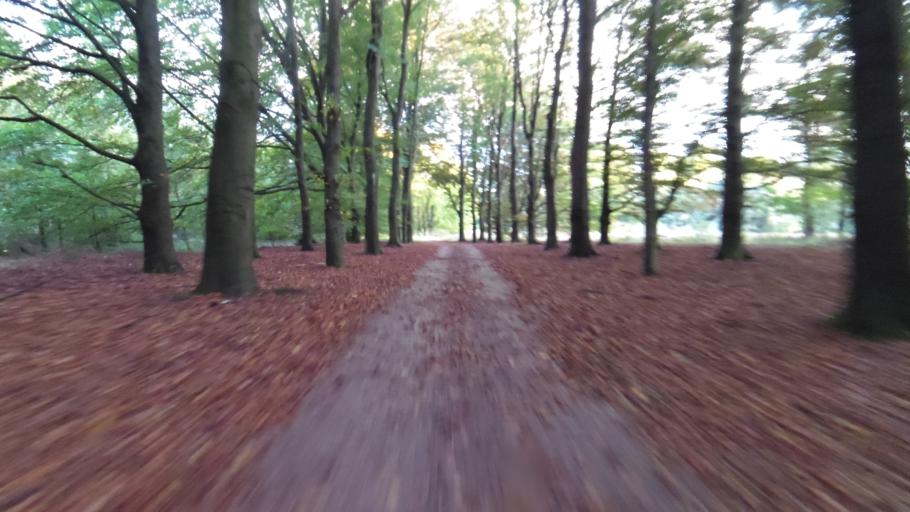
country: NL
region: Gelderland
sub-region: Gemeente Ede
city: Wekerom
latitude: 52.0851
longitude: 5.6927
